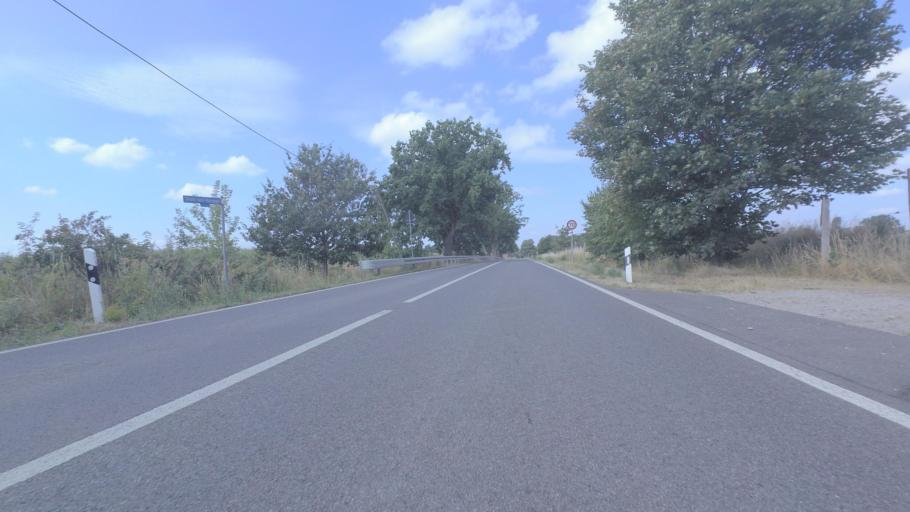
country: DE
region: Brandenburg
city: Walsleben
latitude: 52.9895
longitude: 12.6683
